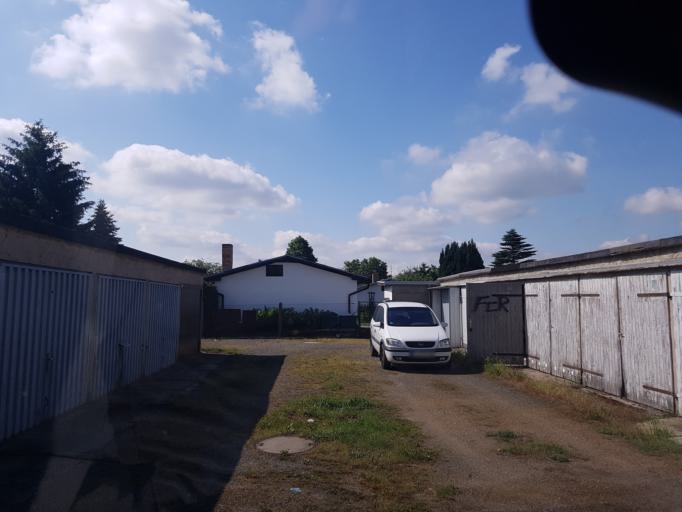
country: DE
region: Brandenburg
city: Finsterwalde
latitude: 51.6212
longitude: 13.7040
